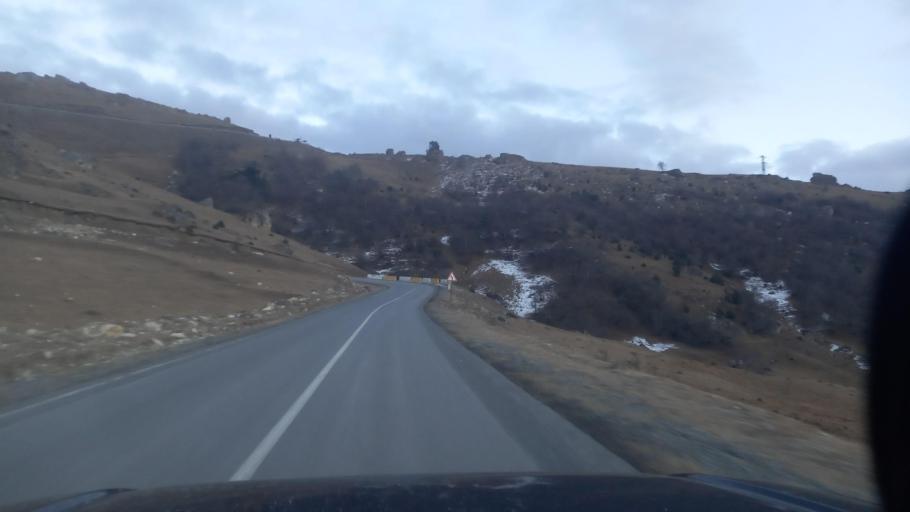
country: RU
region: Ingushetiya
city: Dzhayrakh
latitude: 42.8209
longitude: 44.8255
